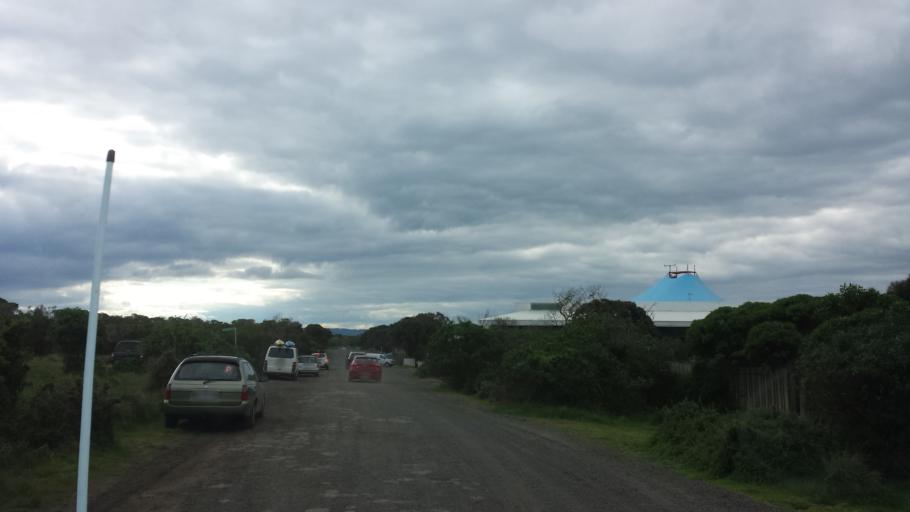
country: AU
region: Victoria
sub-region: Bass Coast
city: Phillip Island
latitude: -38.5099
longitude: 145.1480
